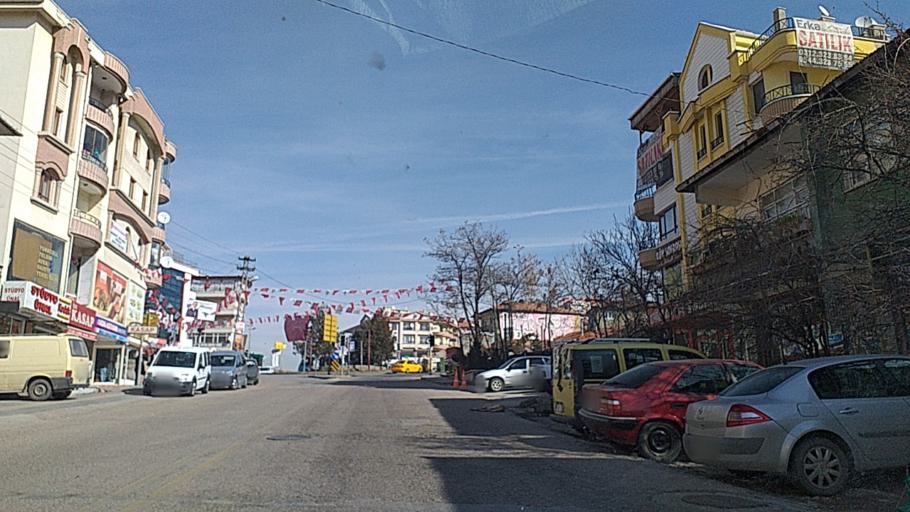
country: TR
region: Ankara
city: Batikent
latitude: 39.9946
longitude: 32.8108
